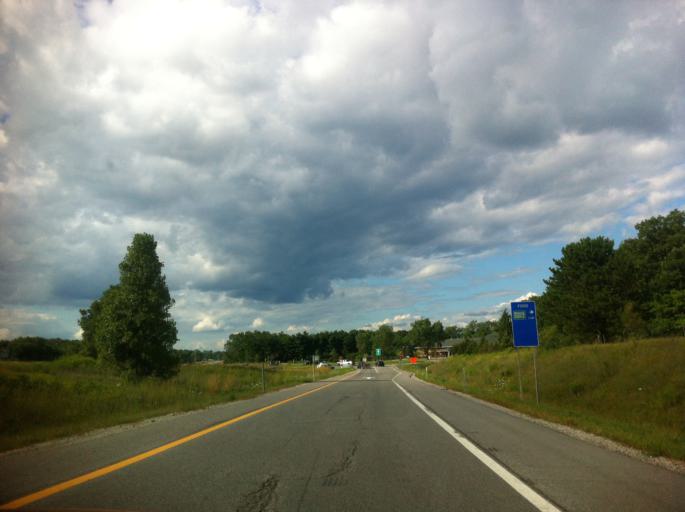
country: US
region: Michigan
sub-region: Livingston County
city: Whitmore Lake
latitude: 42.4655
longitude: -83.7554
